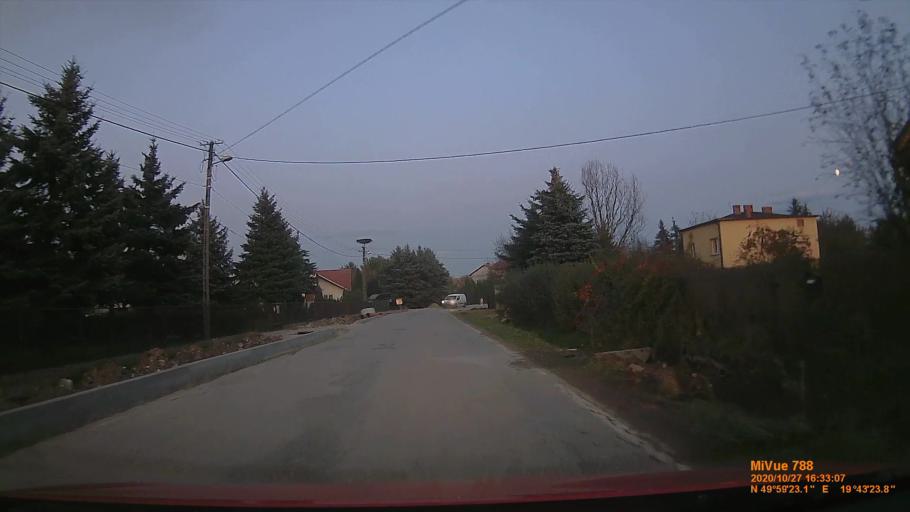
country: PL
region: Lesser Poland Voivodeship
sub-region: Powiat krakowski
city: Wolowice
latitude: 49.9898
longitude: 19.7233
